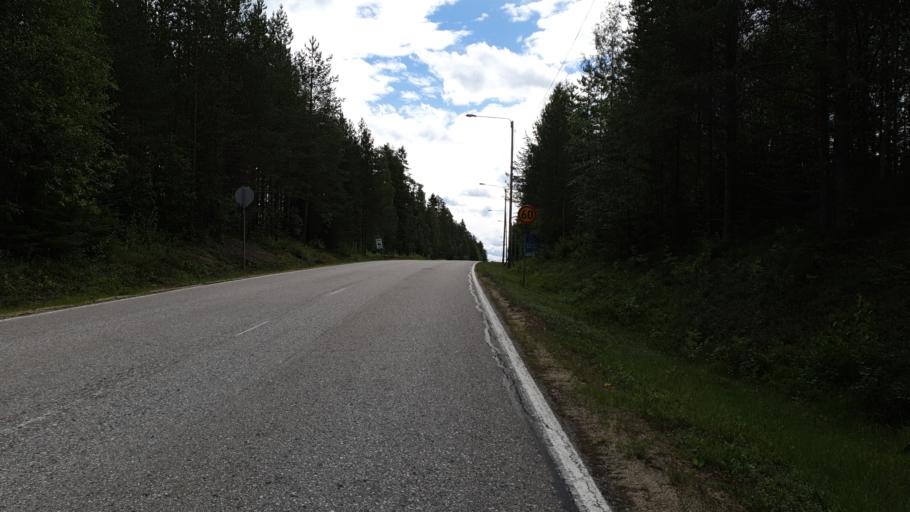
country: FI
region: Kainuu
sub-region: Kehys-Kainuu
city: Kuhmo
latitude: 64.3936
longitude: 29.8299
